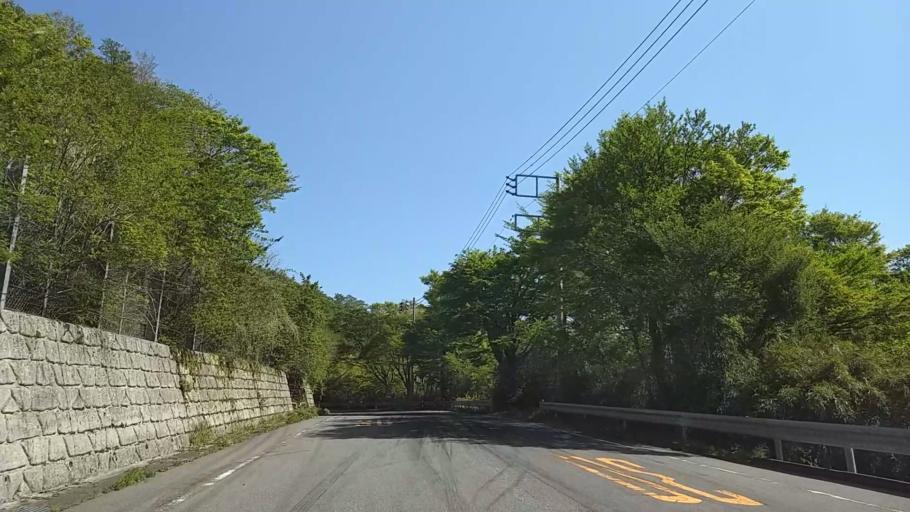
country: JP
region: Shizuoka
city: Gotemba
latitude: 35.2628
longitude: 138.9698
